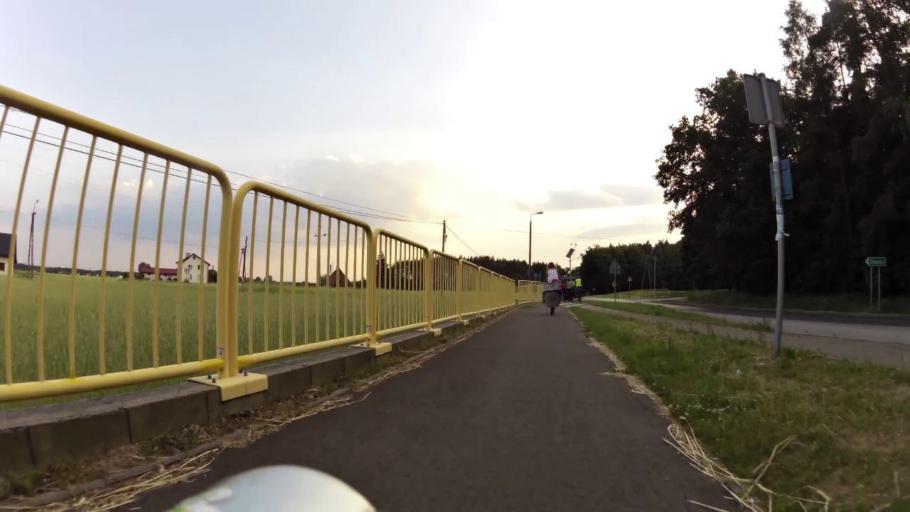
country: PL
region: Kujawsko-Pomorskie
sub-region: Powiat bydgoski
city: Dabrowa Chelminska
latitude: 53.1780
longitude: 18.3255
